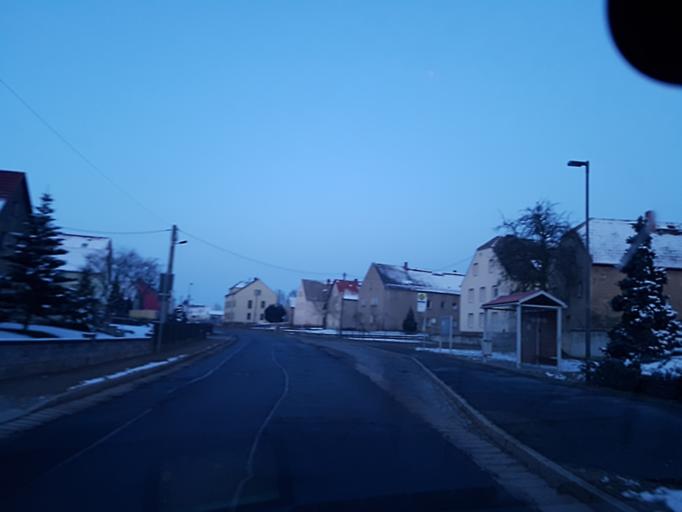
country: DE
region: Saxony
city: Cavertitz
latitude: 51.3657
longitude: 13.1465
